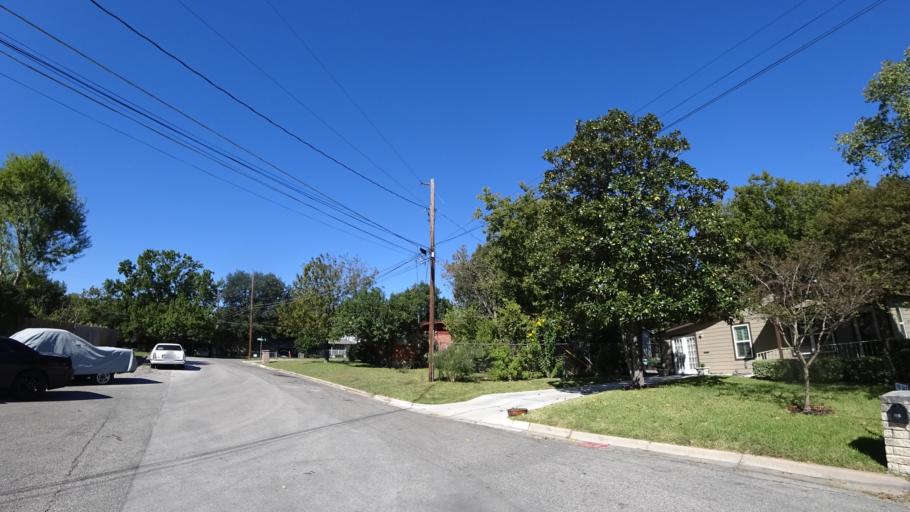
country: US
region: Texas
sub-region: Travis County
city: Austin
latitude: 30.2819
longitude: -97.6813
